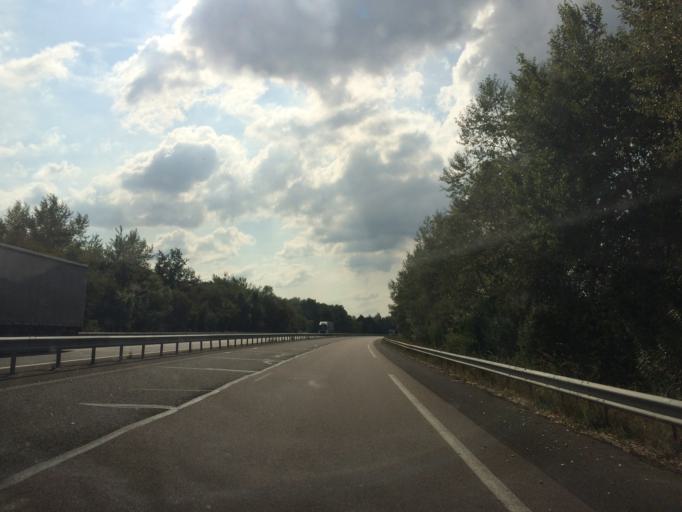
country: FR
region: Lower Normandy
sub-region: Departement de l'Orne
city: Mortagne-au-Perche
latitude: 48.5112
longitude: 0.4171
